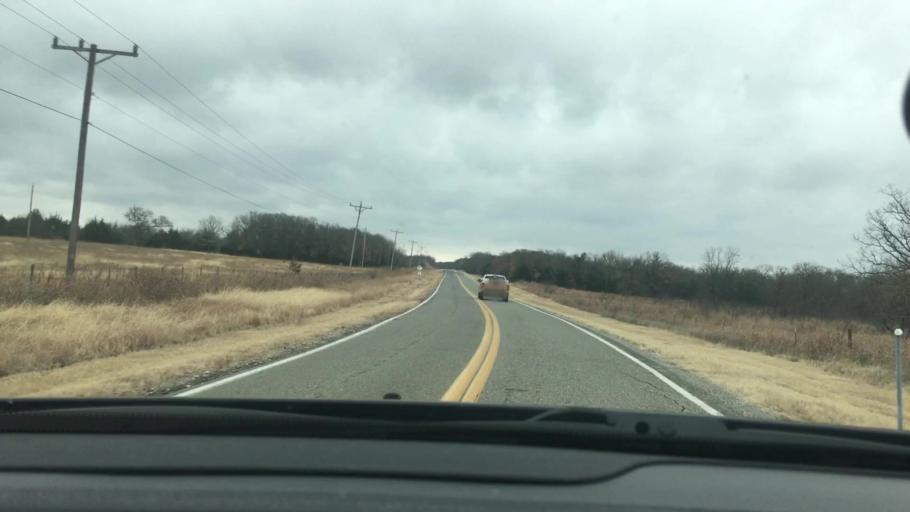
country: US
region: Oklahoma
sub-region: Johnston County
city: Tishomingo
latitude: 34.1817
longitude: -96.5838
